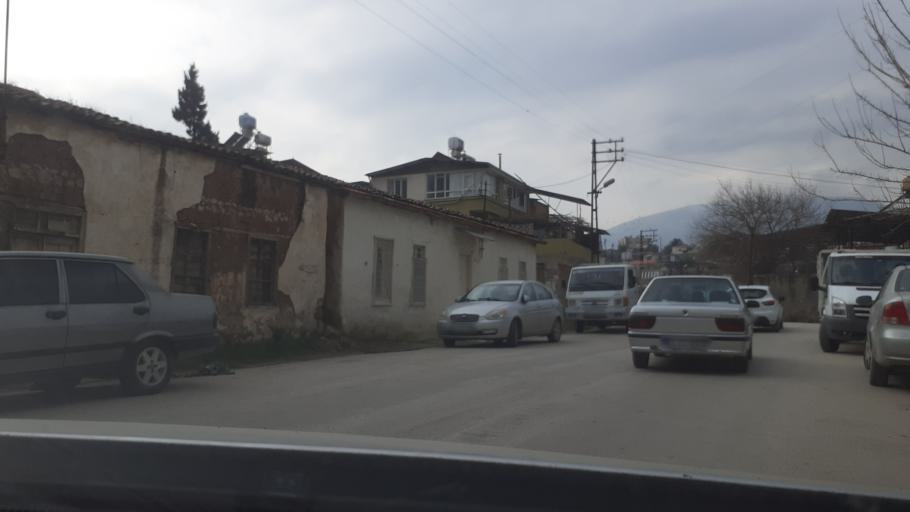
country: TR
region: Hatay
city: Kirikhan
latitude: 36.4965
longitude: 36.3536
